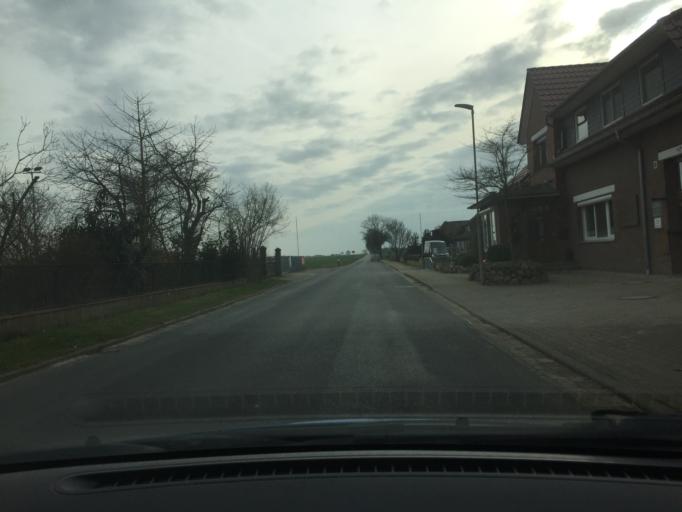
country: DE
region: Lower Saxony
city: Oetzen
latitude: 53.0051
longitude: 10.6740
